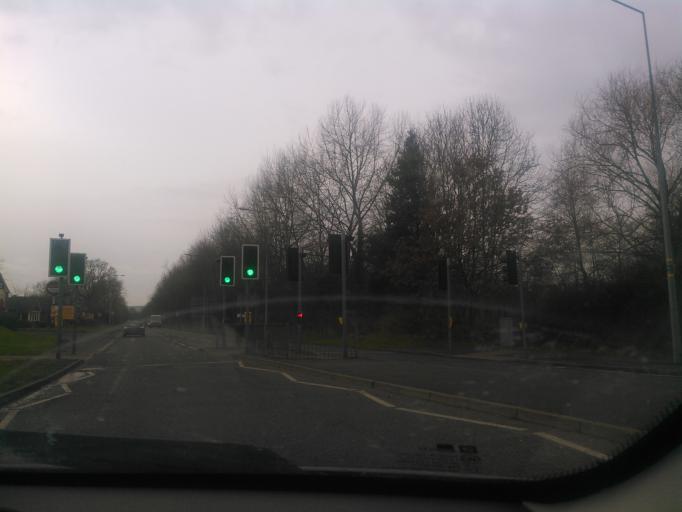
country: GB
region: England
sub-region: Telford and Wrekin
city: Oakengates
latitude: 52.7256
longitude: -2.4345
